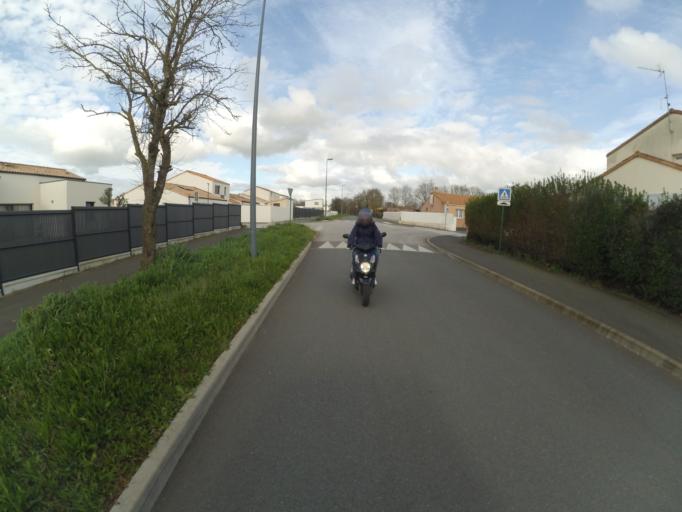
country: FR
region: Pays de la Loire
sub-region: Departement de la Vendee
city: Bouffere
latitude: 46.9657
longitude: -1.3413
